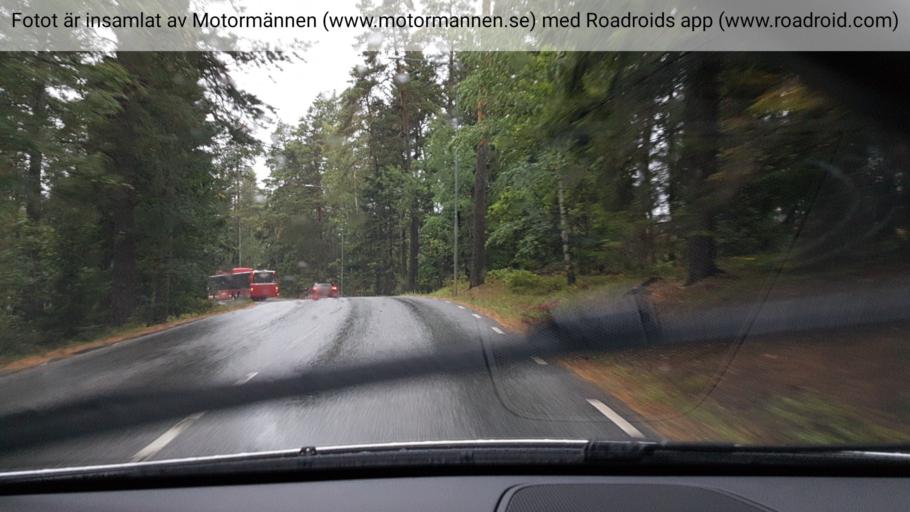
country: SE
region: Stockholm
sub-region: Lidingo
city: Lidingoe
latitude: 59.3807
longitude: 18.1228
